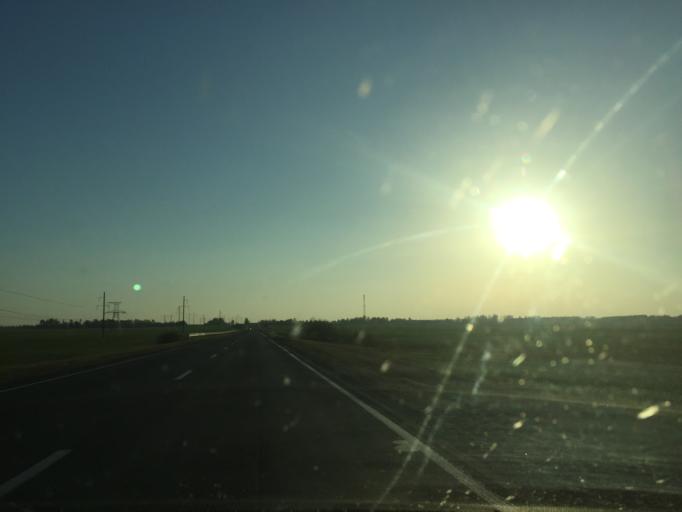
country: BY
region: Mogilev
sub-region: Mahilyowski Rayon
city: Kadino
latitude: 53.8226
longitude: 30.4694
